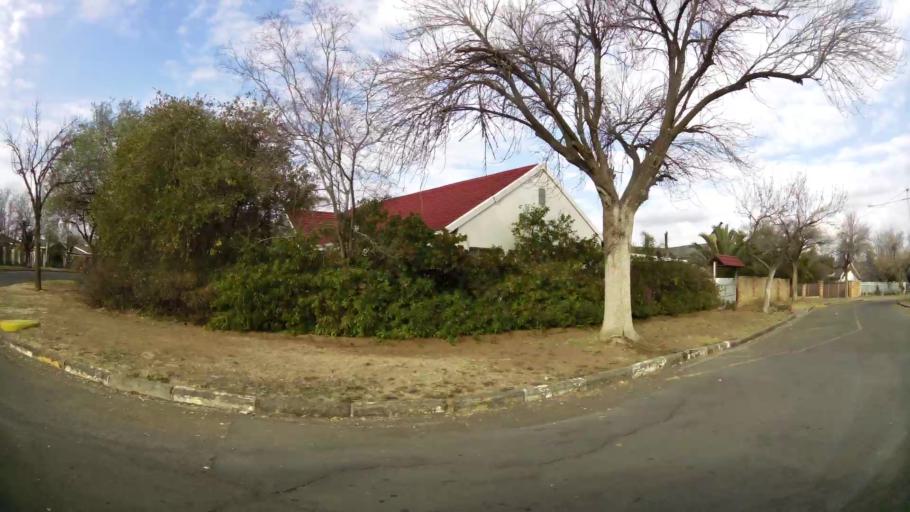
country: ZA
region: Orange Free State
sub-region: Mangaung Metropolitan Municipality
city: Bloemfontein
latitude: -29.0829
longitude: 26.2092
